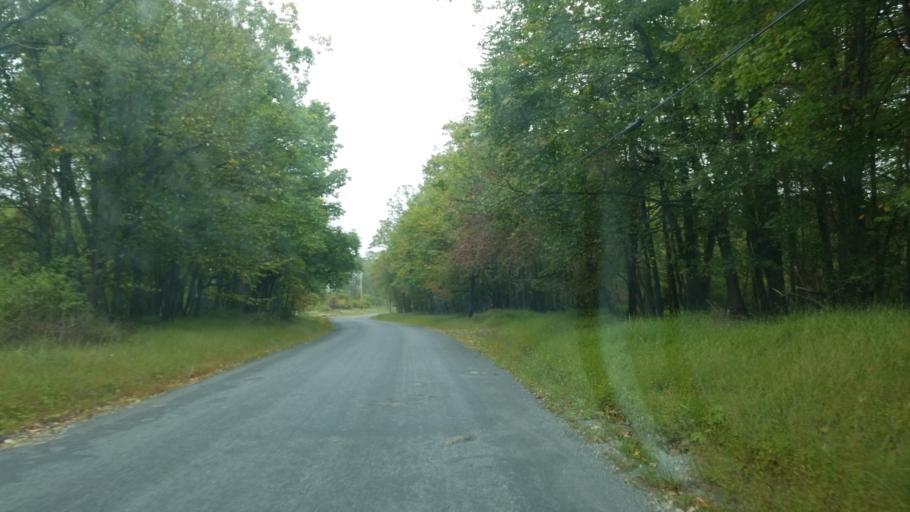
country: US
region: Pennsylvania
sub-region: Clearfield County
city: Curwensville
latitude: 41.0327
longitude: -78.5594
